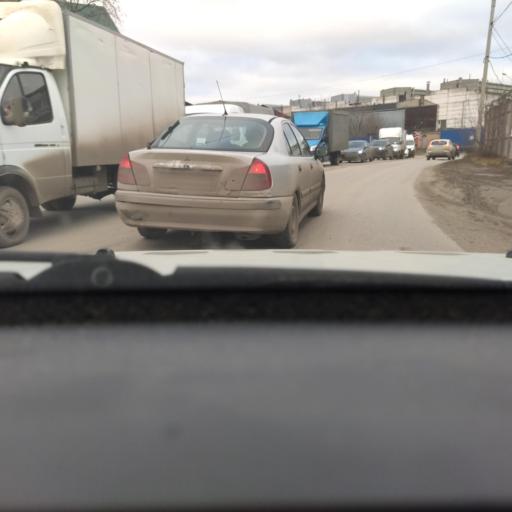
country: RU
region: Perm
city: Perm
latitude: 57.9676
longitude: 56.2531
